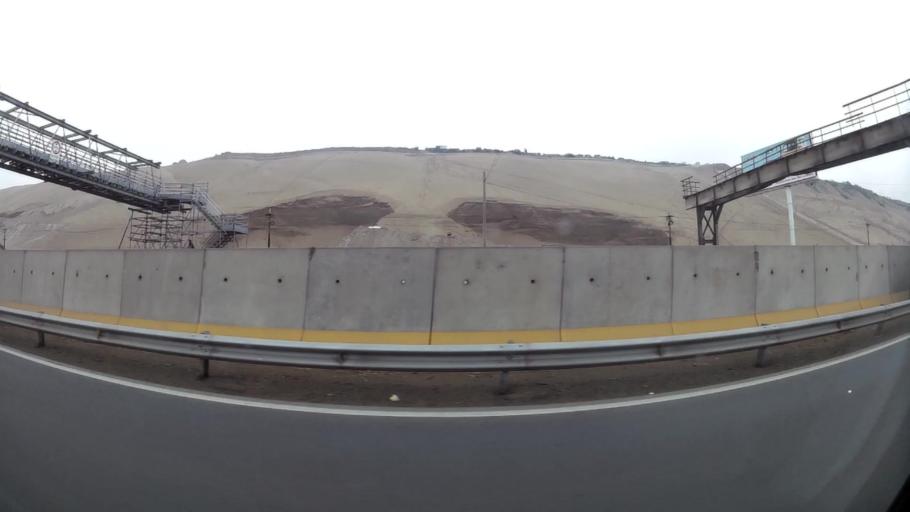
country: PE
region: Lima
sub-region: Lima
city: Surco
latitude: -12.2427
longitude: -76.9436
